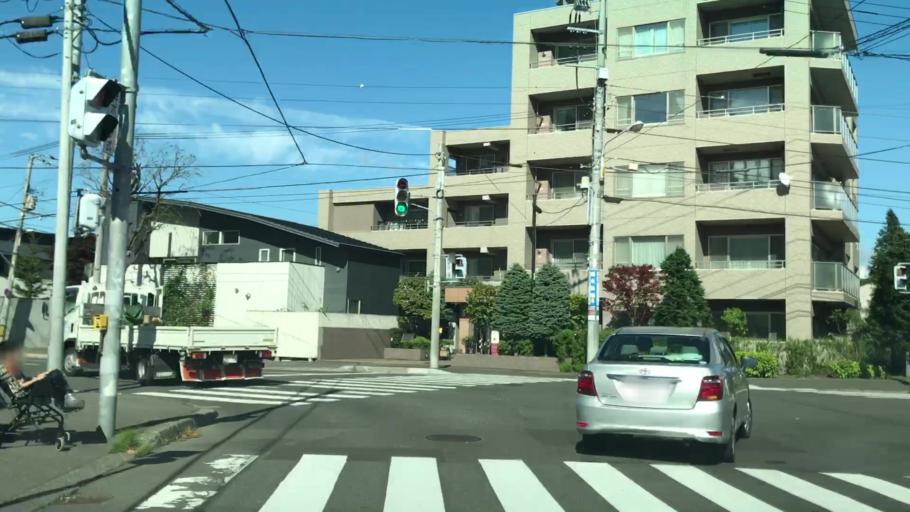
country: JP
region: Hokkaido
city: Sapporo
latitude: 43.0407
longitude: 141.3294
